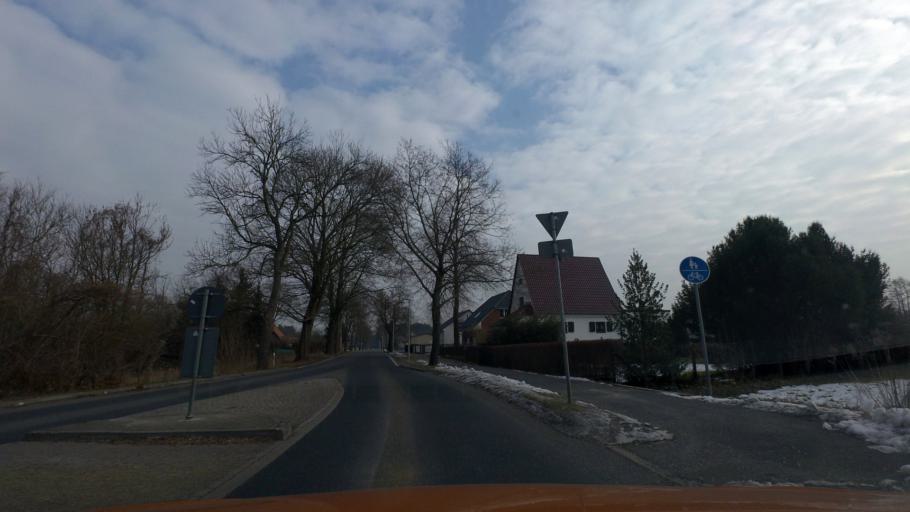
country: DE
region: Brandenburg
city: Zossen
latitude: 52.2454
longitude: 13.4158
